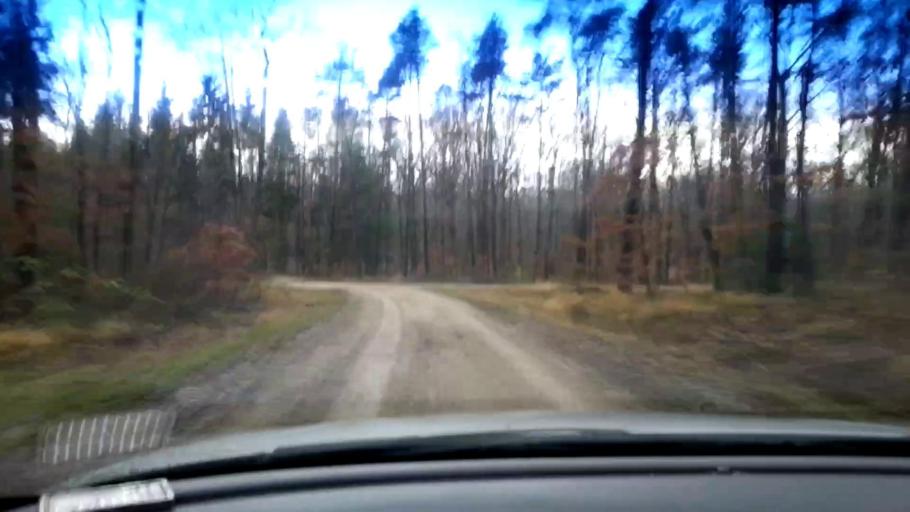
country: DE
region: Bavaria
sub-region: Upper Franconia
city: Gundelsheim
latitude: 49.9548
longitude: 10.9062
